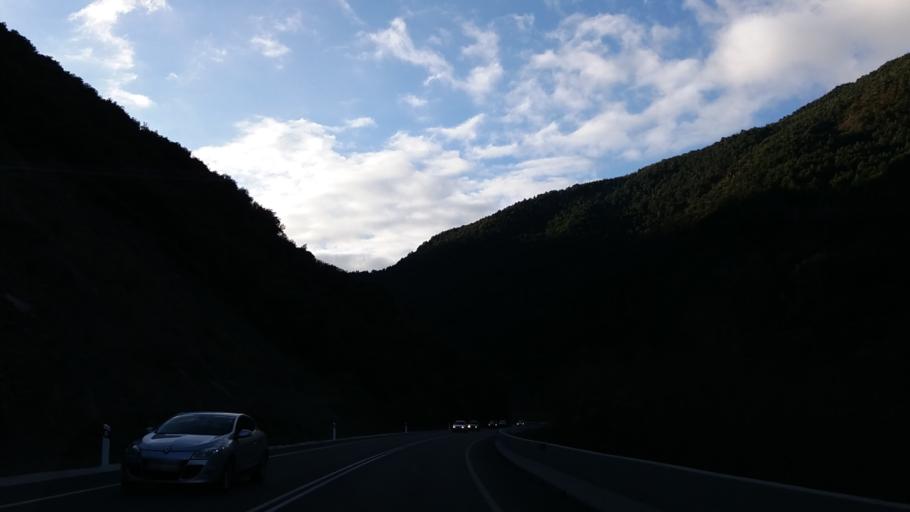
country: AD
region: Sant Julia de Loria
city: Sant Julia de Loria
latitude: 42.4170
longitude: 1.4650
